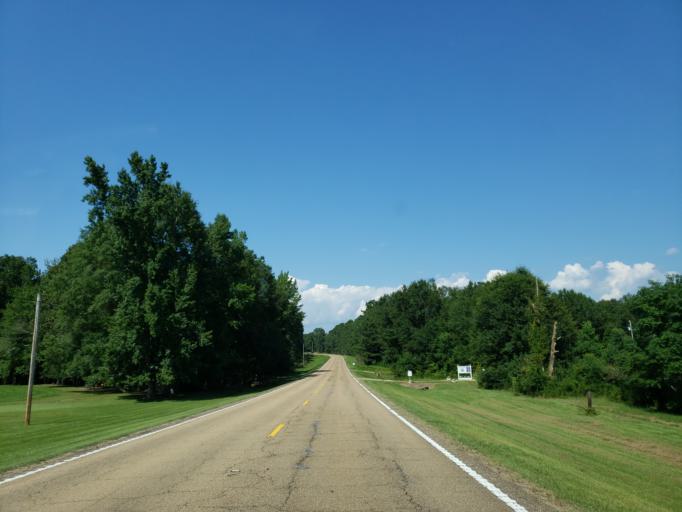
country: US
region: Mississippi
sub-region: Lamar County
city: Sumrall
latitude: 31.4364
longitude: -89.5367
